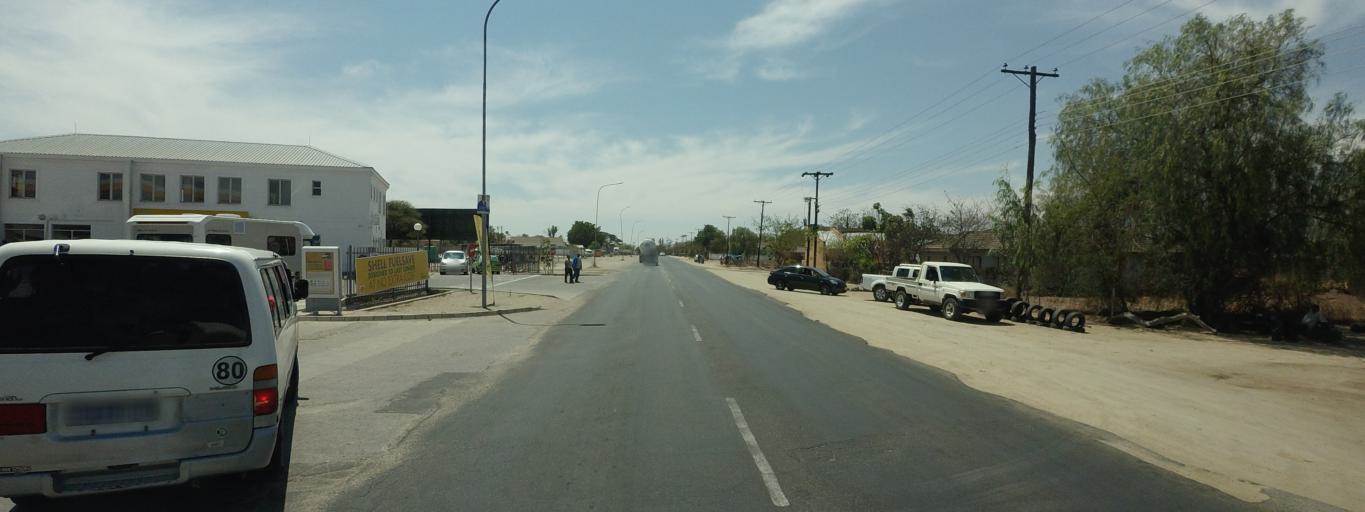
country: BW
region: North East
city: Francistown
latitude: -21.1673
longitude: 27.4951
